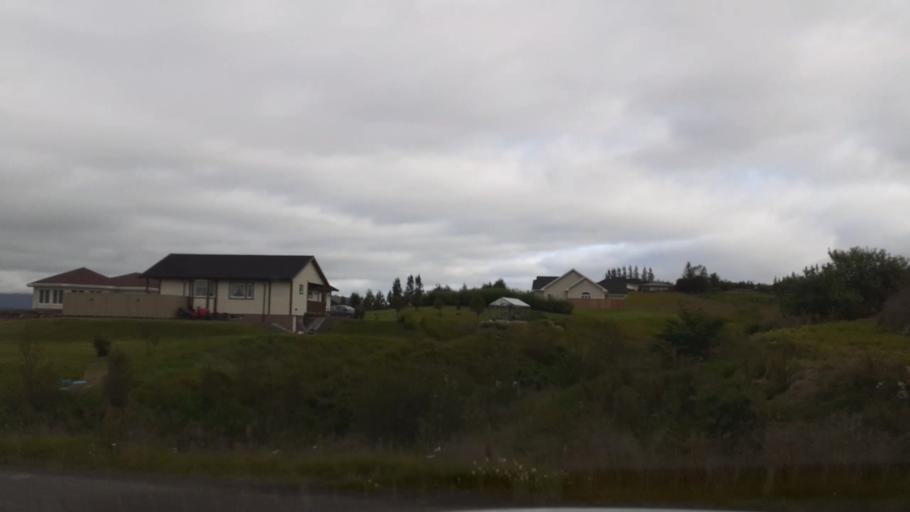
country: IS
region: Northeast
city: Akureyri
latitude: 65.6793
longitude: -18.0377
